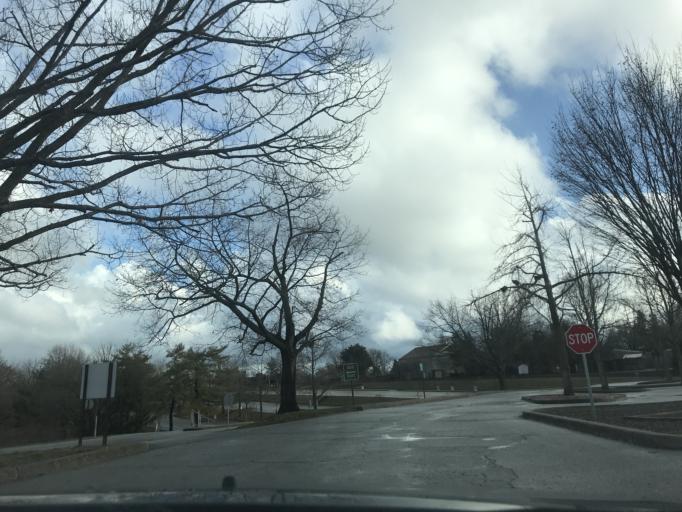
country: US
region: Kentucky
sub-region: Jefferson County
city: Audubon Park
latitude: 38.2074
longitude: -85.7068
